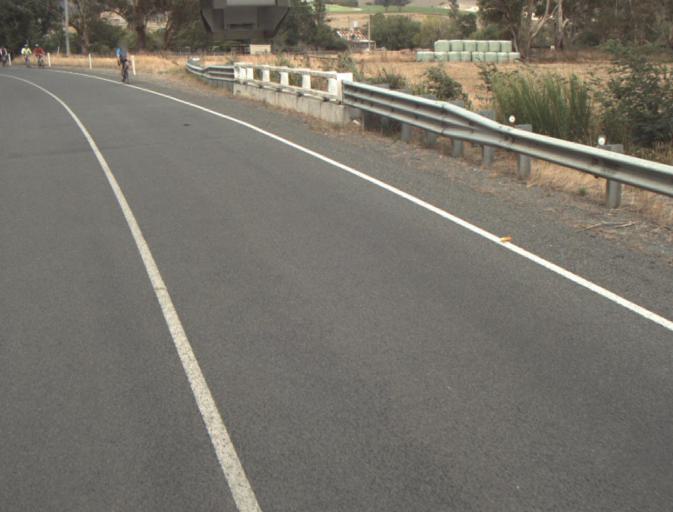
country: AU
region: Tasmania
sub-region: Launceston
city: Mayfield
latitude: -41.2286
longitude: 147.2090
